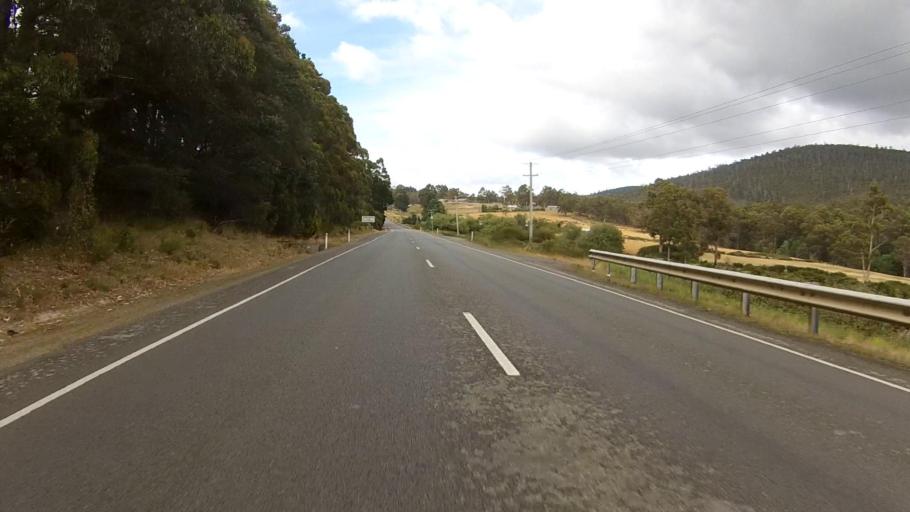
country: AU
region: Tasmania
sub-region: Kingborough
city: Kettering
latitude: -43.0831
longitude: 147.2535
